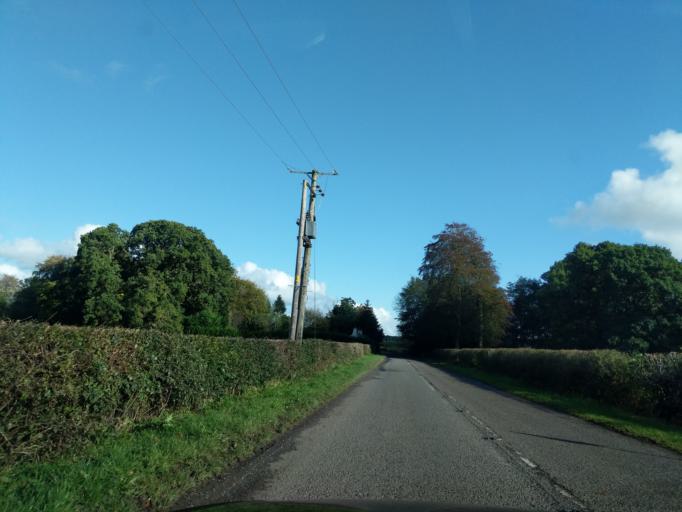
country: GB
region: Scotland
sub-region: Dumfries and Galloway
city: Dumfries
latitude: 55.0608
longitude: -3.6669
